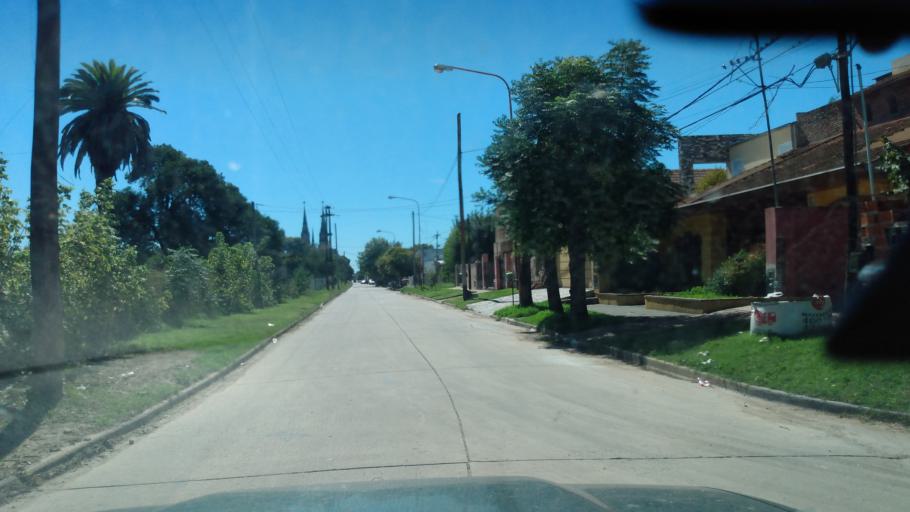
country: AR
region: Buenos Aires
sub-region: Partido de Lujan
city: Lujan
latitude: -34.5724
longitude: -59.1243
